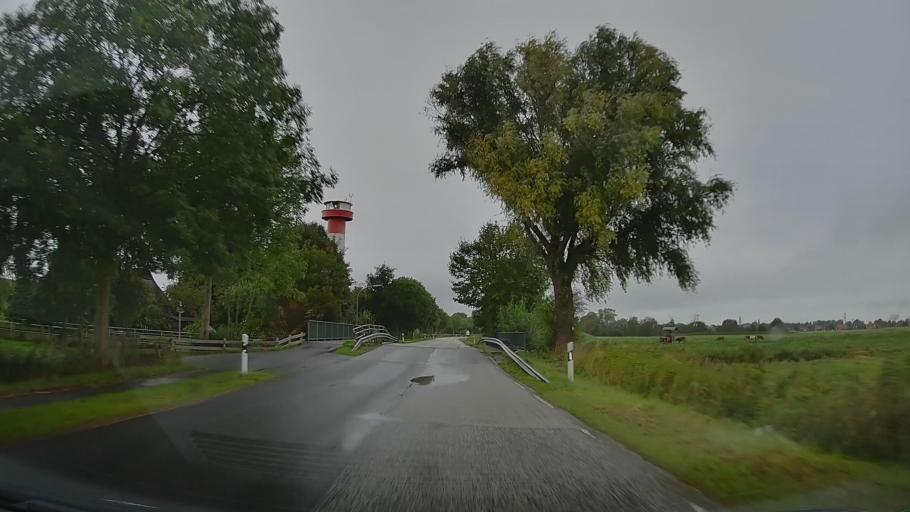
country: DE
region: Schleswig-Holstein
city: Sankt Margarethen
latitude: 53.8805
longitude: 9.2621
